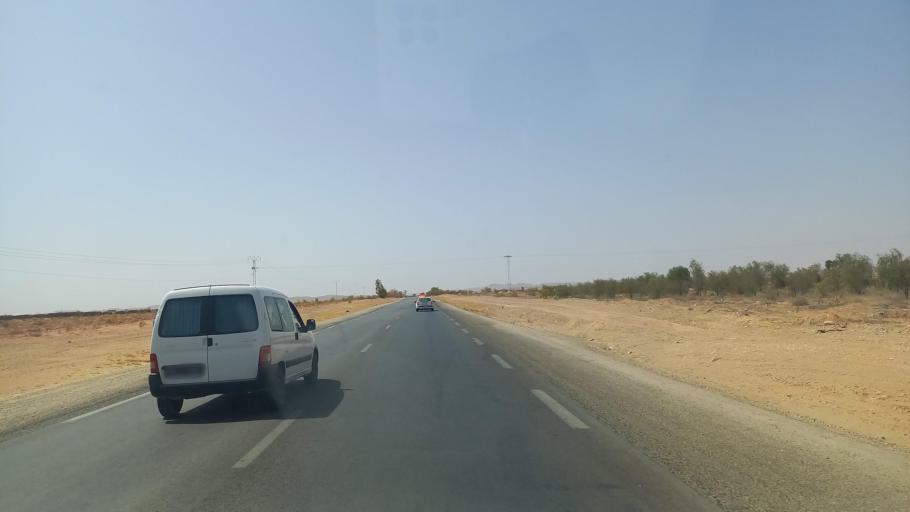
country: TN
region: Madanin
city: Medenine
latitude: 33.2208
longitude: 10.4497
